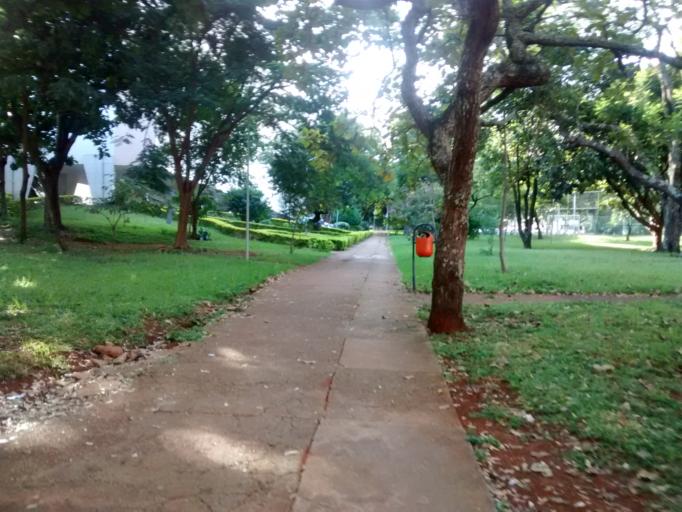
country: BR
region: Federal District
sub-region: Brasilia
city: Brasilia
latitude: -15.8141
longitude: -47.9002
